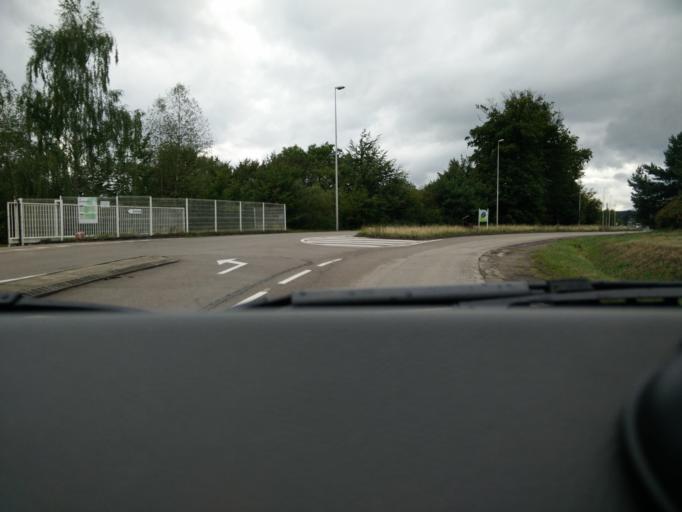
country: FR
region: Lorraine
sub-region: Departement des Vosges
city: Saint-Die-des-Vosges
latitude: 48.3009
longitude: 6.9286
